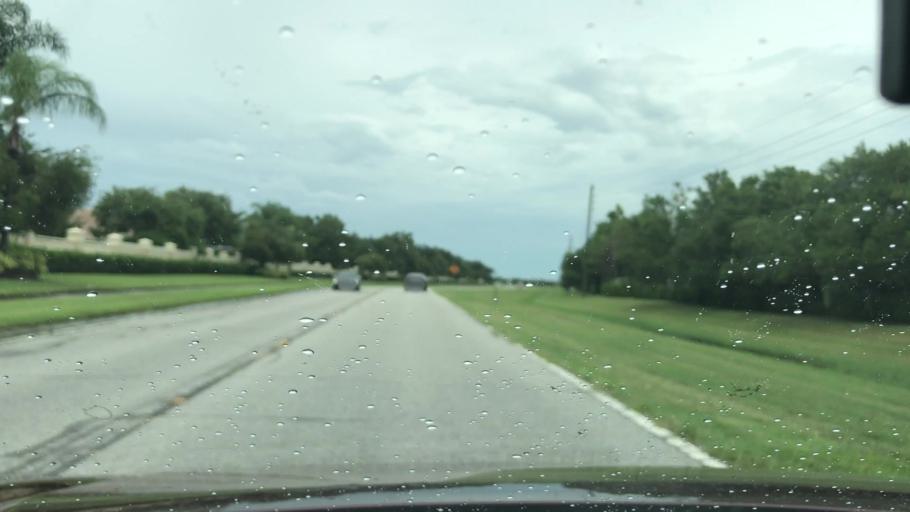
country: US
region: Florida
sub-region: Sarasota County
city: Lake Sarasota
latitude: 27.3091
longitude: -82.3952
